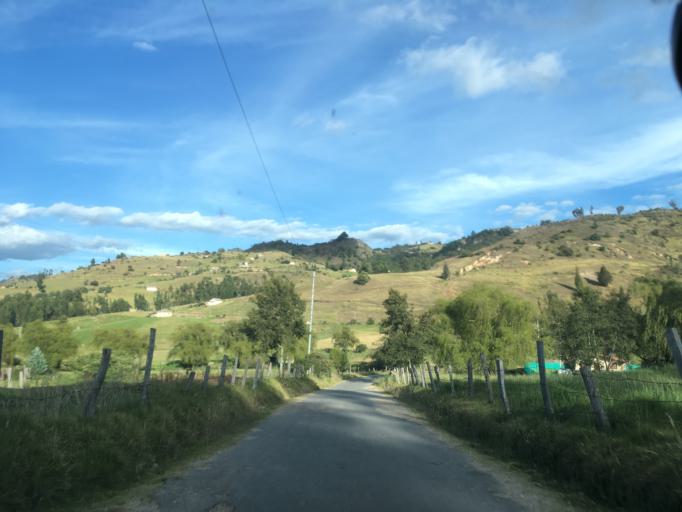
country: CO
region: Boyaca
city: Pesca
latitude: 5.5484
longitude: -73.0573
